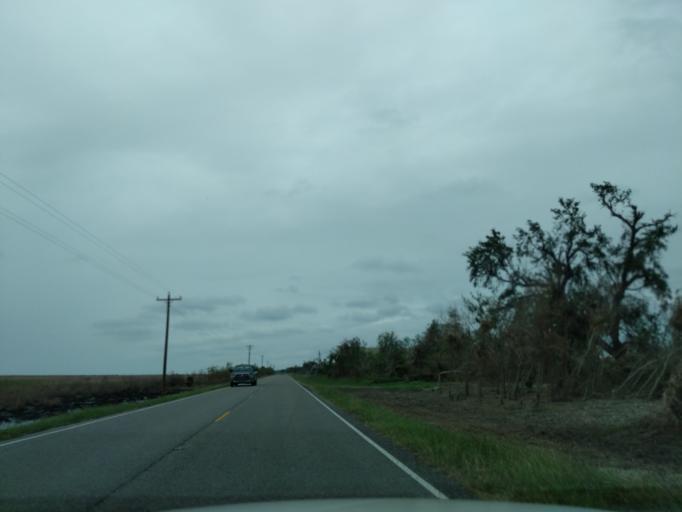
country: US
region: Louisiana
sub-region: Cameron Parish
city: Cameron
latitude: 29.7869
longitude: -93.1475
